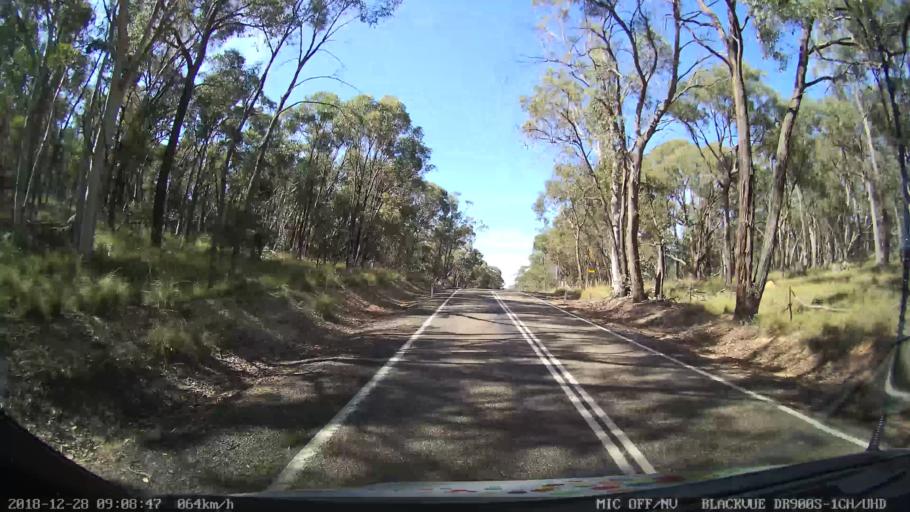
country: AU
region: New South Wales
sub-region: Upper Lachlan Shire
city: Crookwell
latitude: -34.2152
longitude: 149.3370
